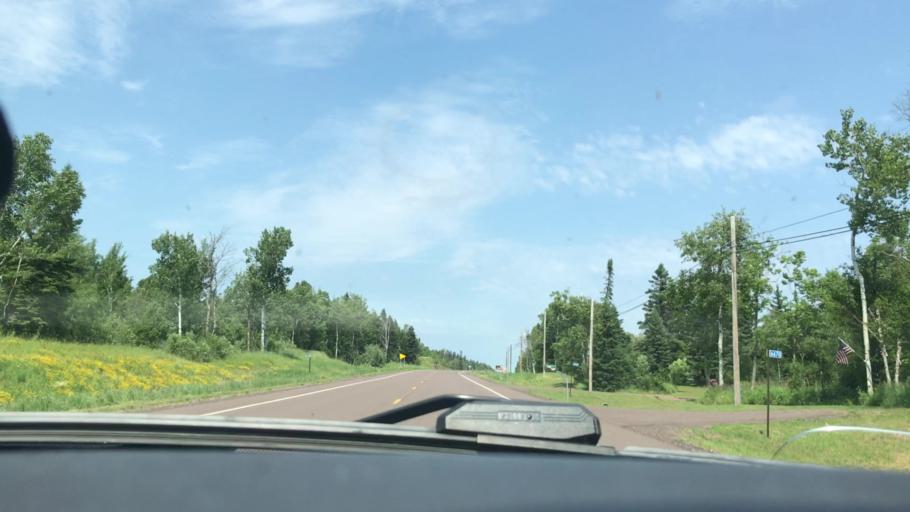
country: US
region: Minnesota
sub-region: Lake County
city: Silver Bay
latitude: 47.4280
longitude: -91.0894
